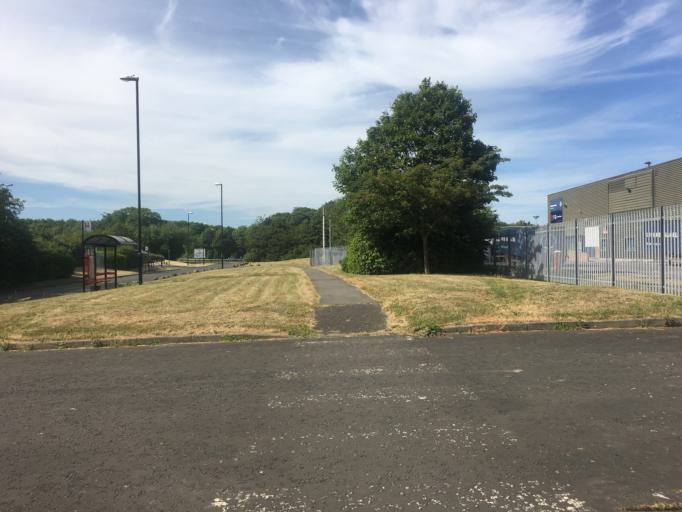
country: GB
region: England
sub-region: Sunderland
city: Washington
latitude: 54.8857
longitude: -1.5388
